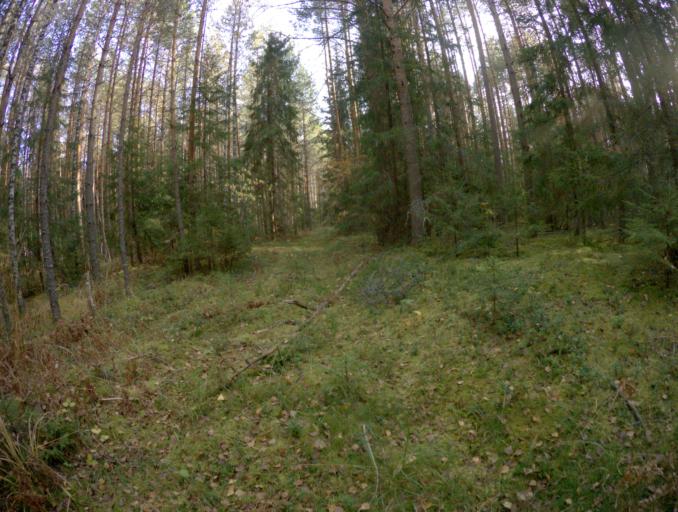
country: RU
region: Vladimir
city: Sobinka
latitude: 55.9392
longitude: 40.0339
